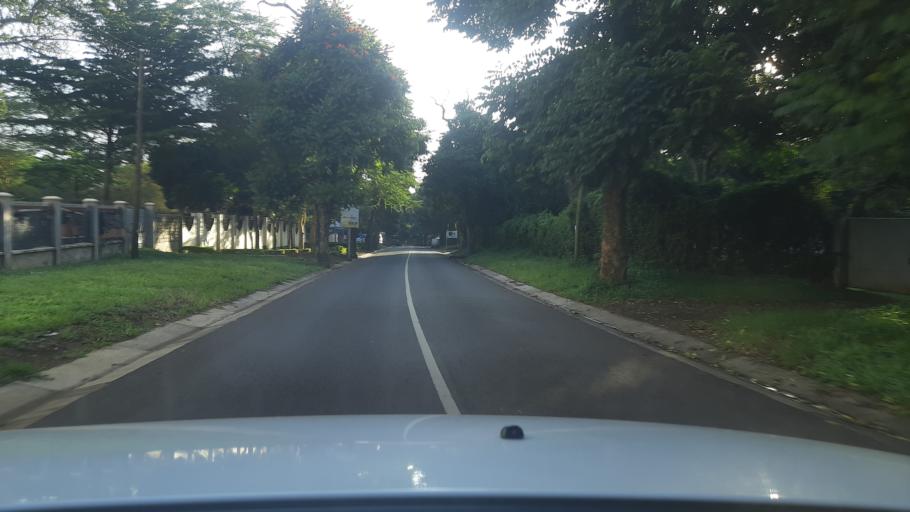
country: TZ
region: Arusha
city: Arusha
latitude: -3.3783
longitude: 36.7004
